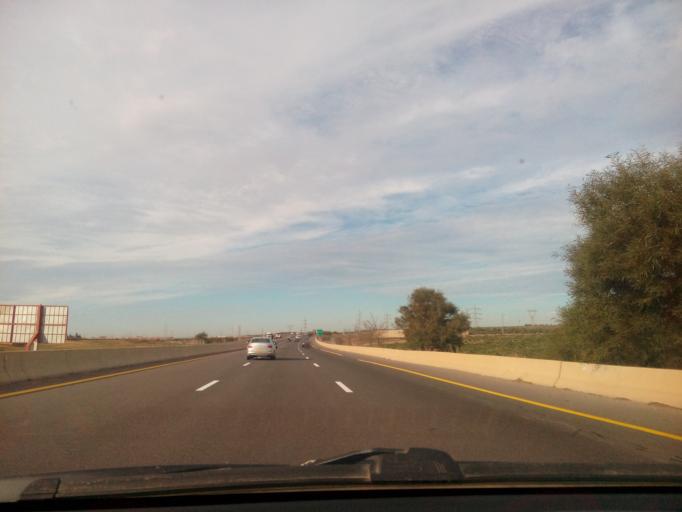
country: DZ
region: Mascara
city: Sig
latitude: 35.5420
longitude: -0.3635
